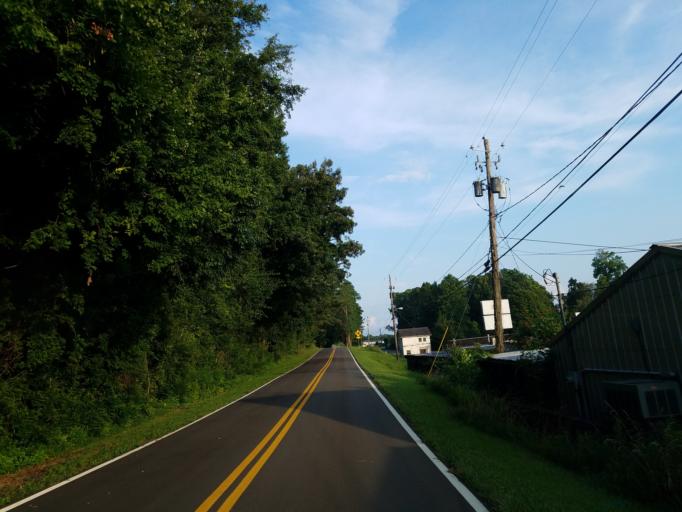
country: US
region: Georgia
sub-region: Pickens County
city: Jasper
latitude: 34.4602
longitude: -84.4127
